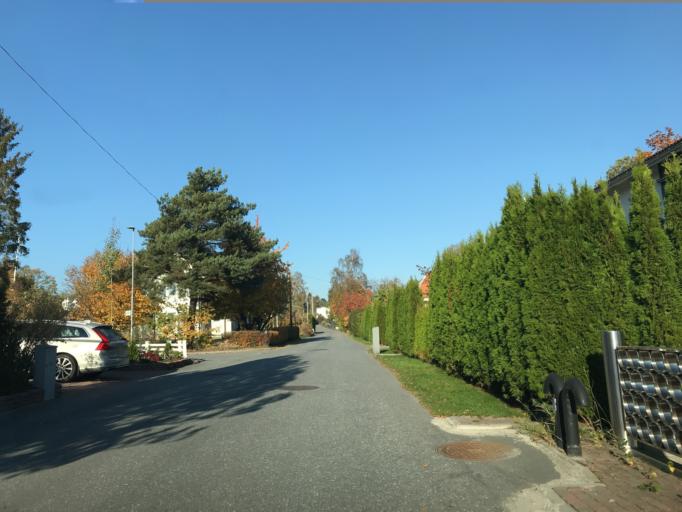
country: SE
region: Stockholm
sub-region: Sollentuna Kommun
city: Sollentuna
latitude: 59.4201
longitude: 17.9371
